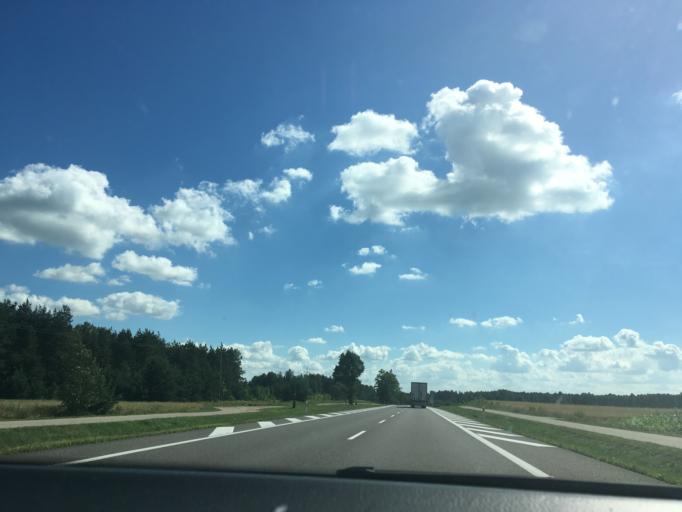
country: PL
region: Podlasie
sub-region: Powiat sokolski
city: Suchowola
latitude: 53.7026
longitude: 23.0951
